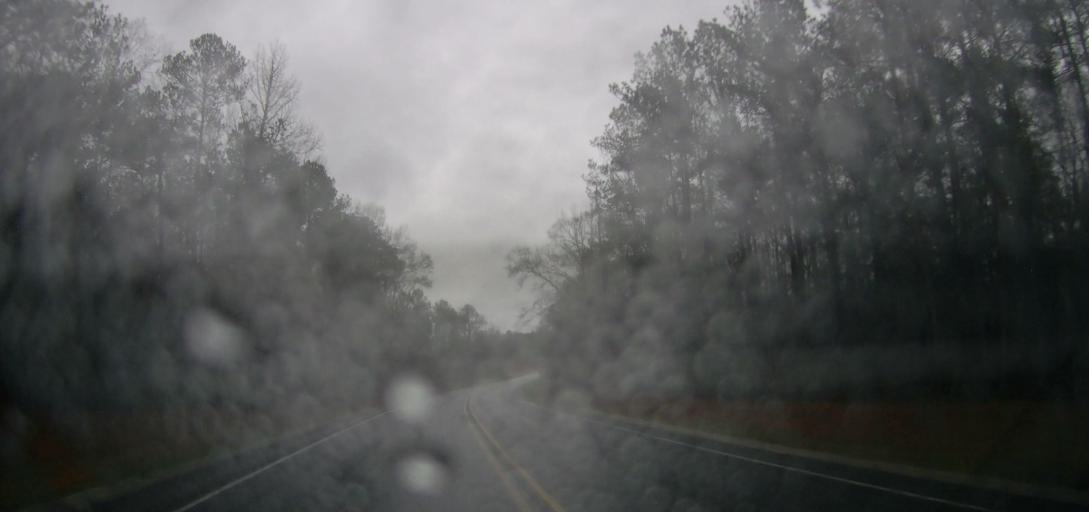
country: US
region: Alabama
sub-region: Chilton County
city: Clanton
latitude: 32.6115
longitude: -86.7196
